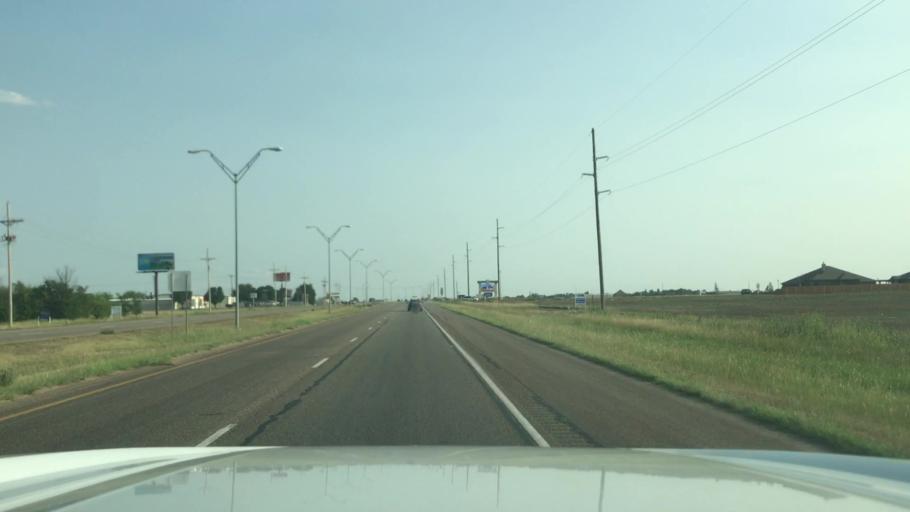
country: US
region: Texas
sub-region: Potter County
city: Bushland
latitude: 35.1284
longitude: -101.9381
